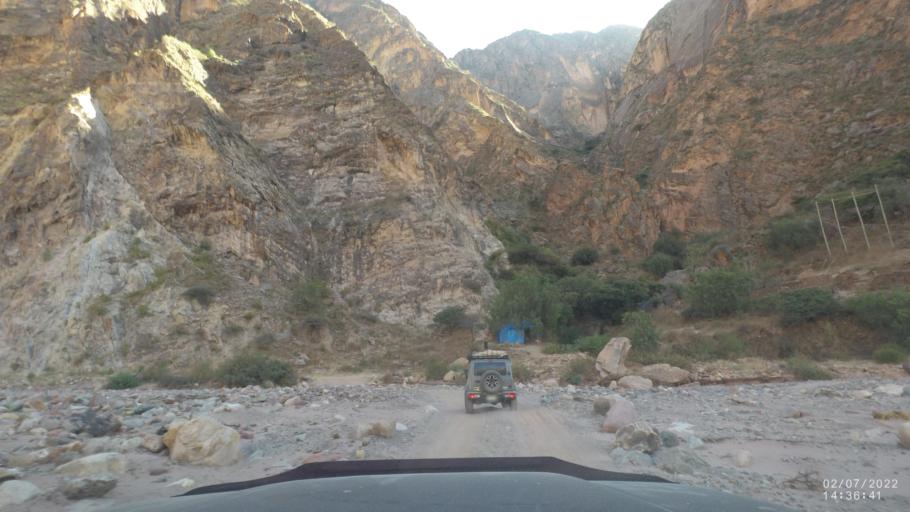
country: BO
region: Cochabamba
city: Irpa Irpa
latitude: -17.8408
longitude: -66.4183
